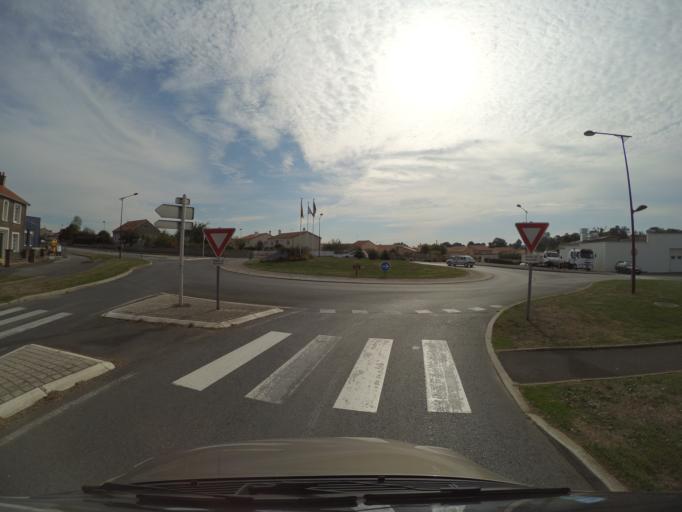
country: FR
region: Pays de la Loire
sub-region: Departement de Maine-et-Loire
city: Jallais
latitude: 47.1970
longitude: -0.8610
